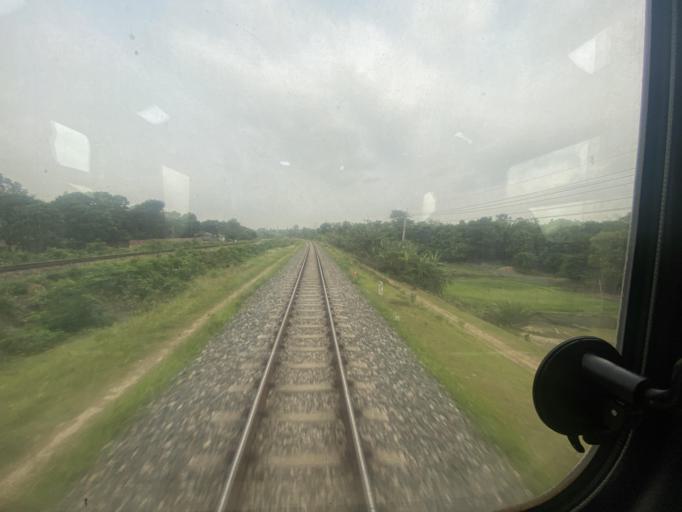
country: BD
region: Dhaka
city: Tungi
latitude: 23.9360
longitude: 90.4870
